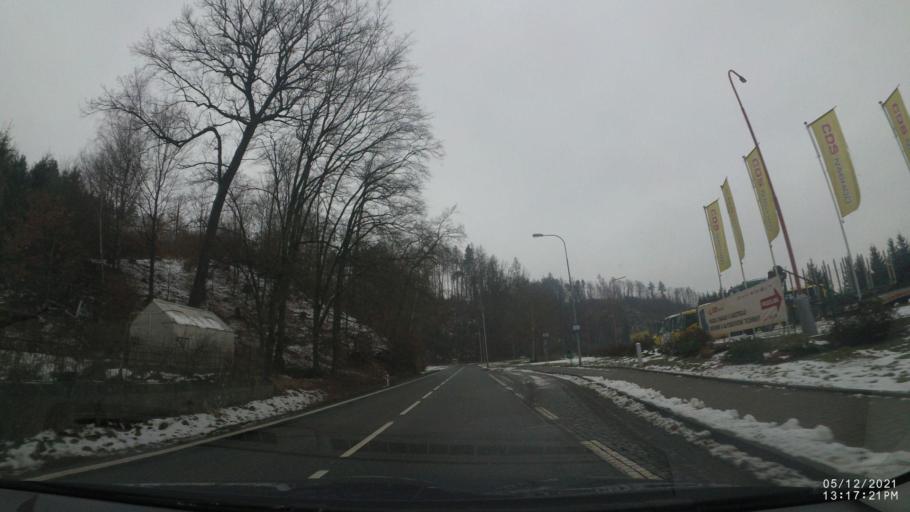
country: CZ
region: Kralovehradecky
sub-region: Okres Nachod
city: Nachod
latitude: 50.4279
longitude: 16.1900
